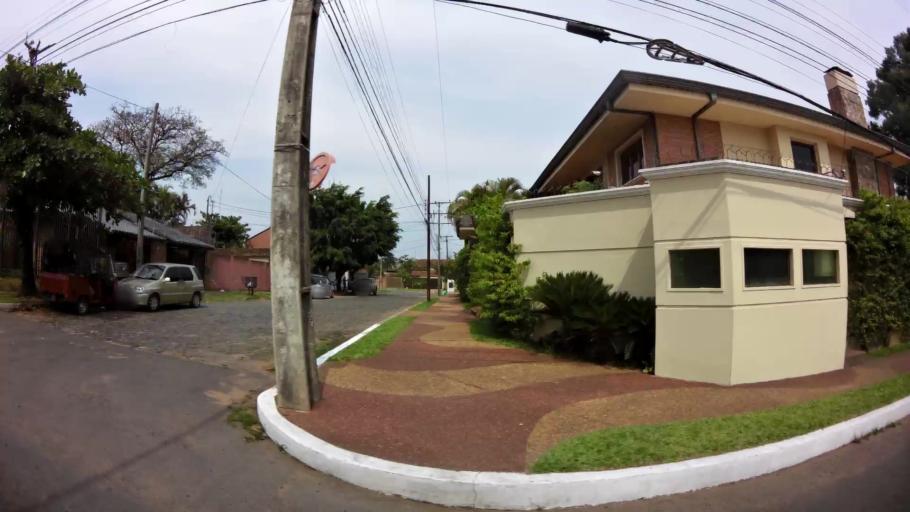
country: PY
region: Asuncion
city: Asuncion
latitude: -25.2759
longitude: -57.5652
